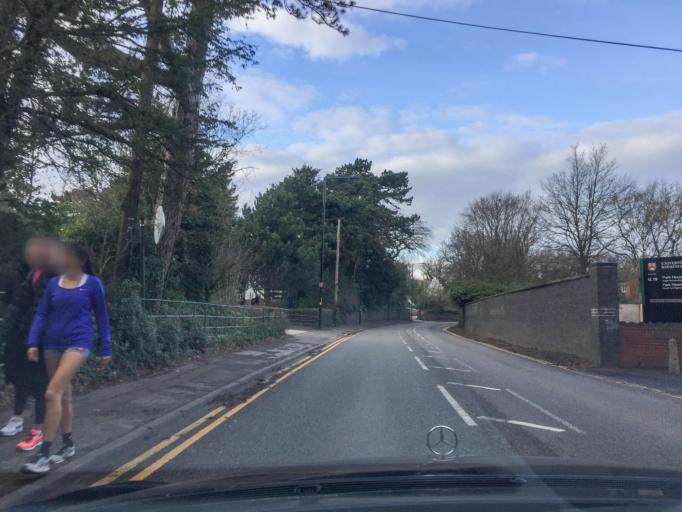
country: GB
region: England
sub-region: City and Borough of Birmingham
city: Birmingham
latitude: 52.4562
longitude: -1.9272
